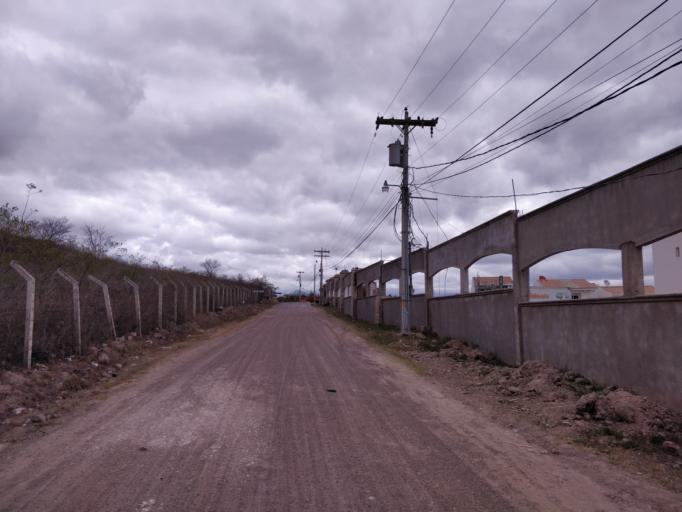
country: HN
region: Francisco Morazan
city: Yaguacire
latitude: 14.0327
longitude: -87.2490
